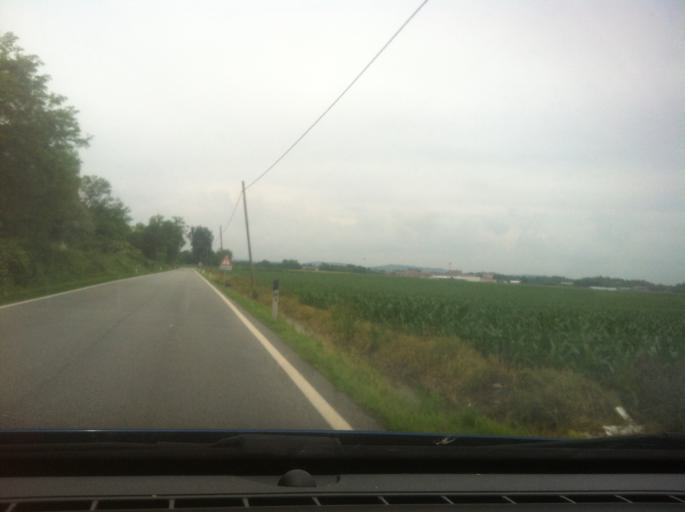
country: IT
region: Piedmont
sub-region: Provincia di Torino
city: Foglizzo
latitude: 45.2556
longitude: 7.8103
